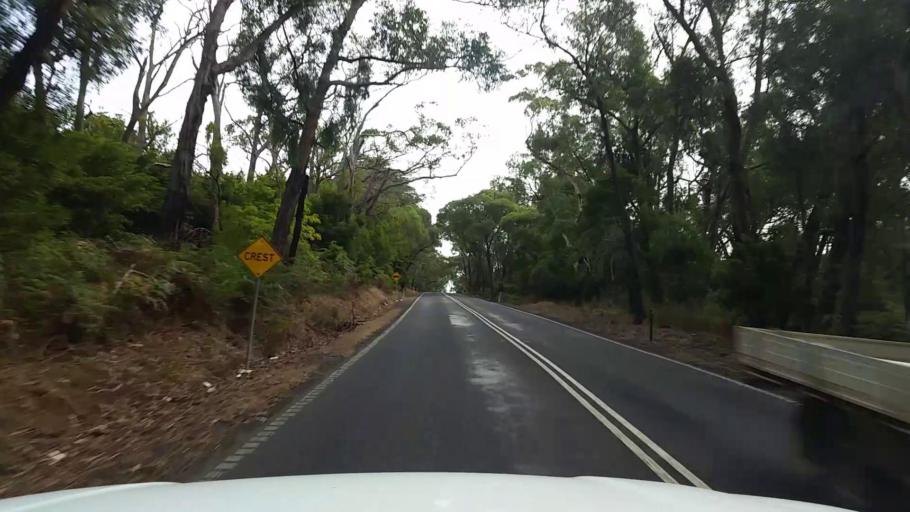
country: AU
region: Victoria
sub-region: Mornington Peninsula
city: Balnarring
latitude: -38.3335
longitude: 145.0952
